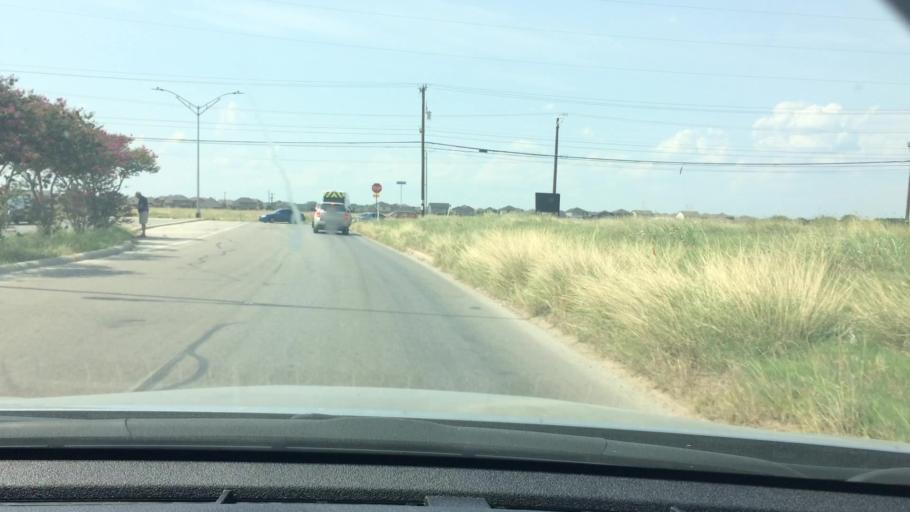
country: US
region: Texas
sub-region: Bexar County
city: Leon Valley
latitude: 29.4464
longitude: -98.6531
